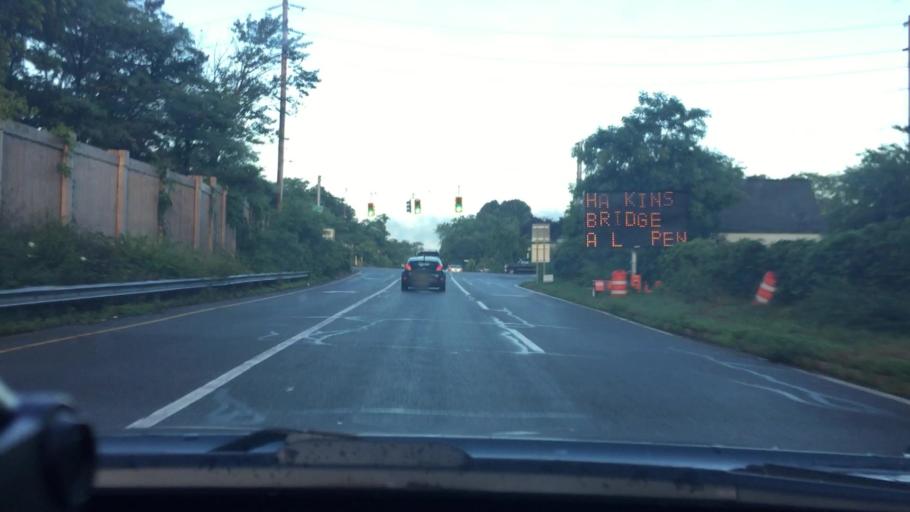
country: US
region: New York
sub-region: Suffolk County
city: Ronkonkoma
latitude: 40.8141
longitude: -73.1072
